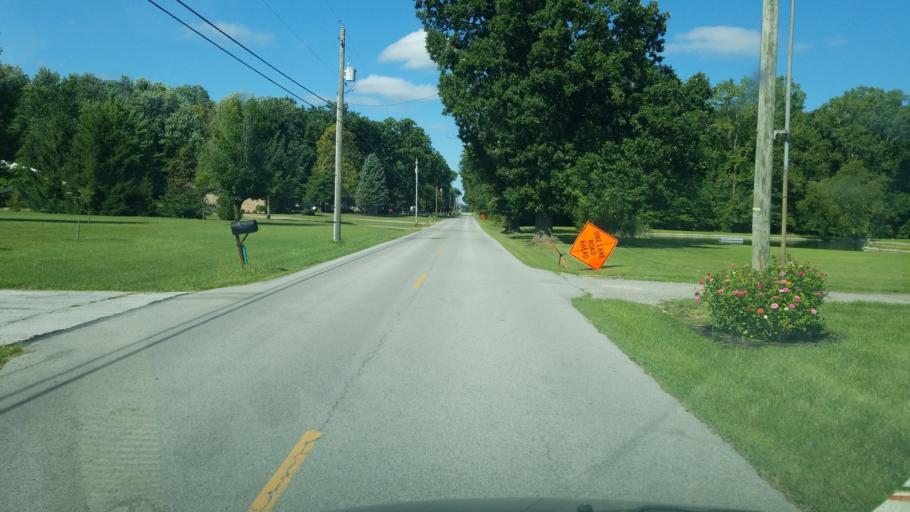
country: US
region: Ohio
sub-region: Hancock County
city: Findlay
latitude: 41.1094
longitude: -83.6383
